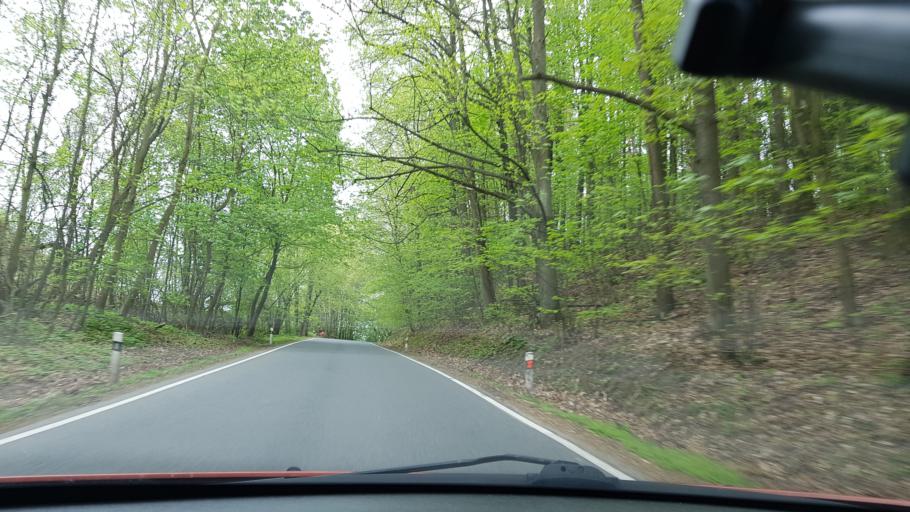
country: CZ
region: Olomoucky
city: Vidnava
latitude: 50.3662
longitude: 17.1955
